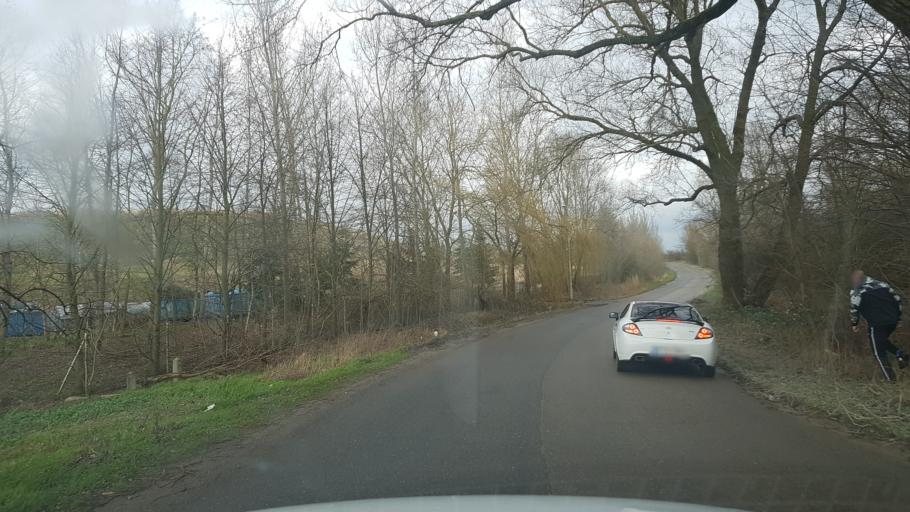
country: PL
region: West Pomeranian Voivodeship
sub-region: Powiat policki
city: Kolbaskowo
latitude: 53.3480
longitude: 14.4388
